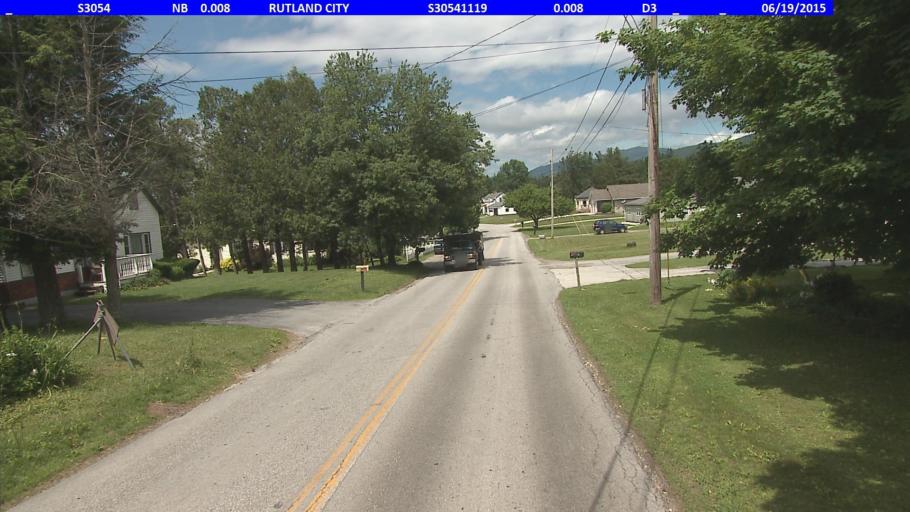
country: US
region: Vermont
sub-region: Rutland County
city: Rutland
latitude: 43.5935
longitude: -72.9500
